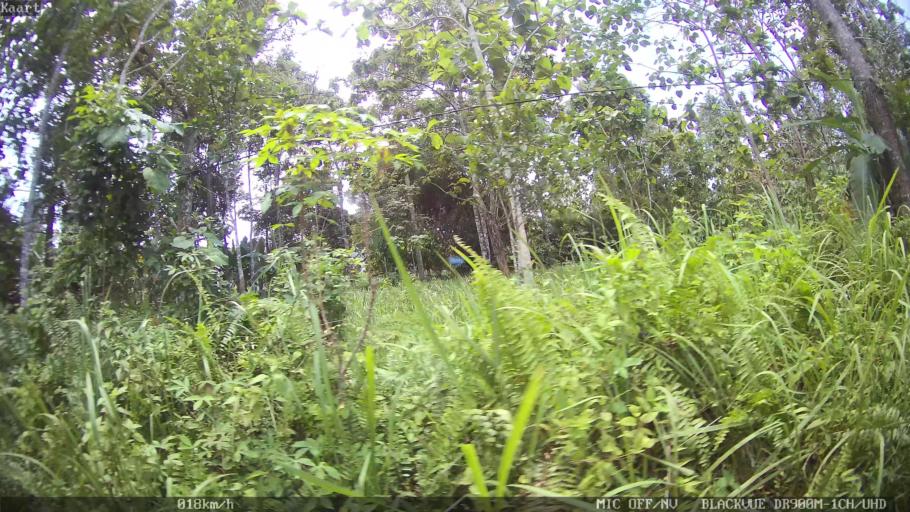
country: ID
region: Lampung
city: Bandarlampung
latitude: -5.4115
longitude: 105.2132
